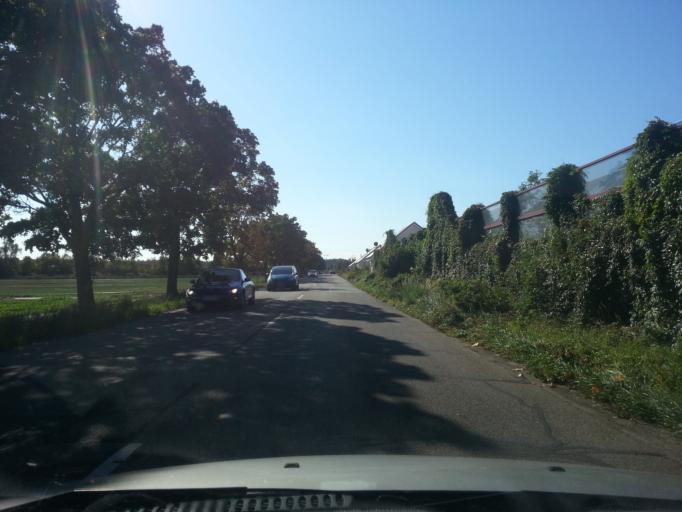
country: DE
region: Rheinland-Pfalz
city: Schifferstadt
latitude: 49.3907
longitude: 8.3884
